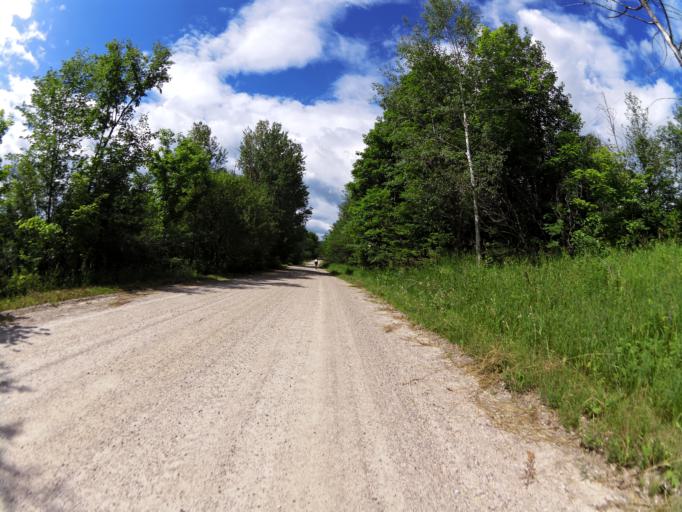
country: CA
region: Ontario
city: Perth
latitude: 45.0294
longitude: -76.5077
